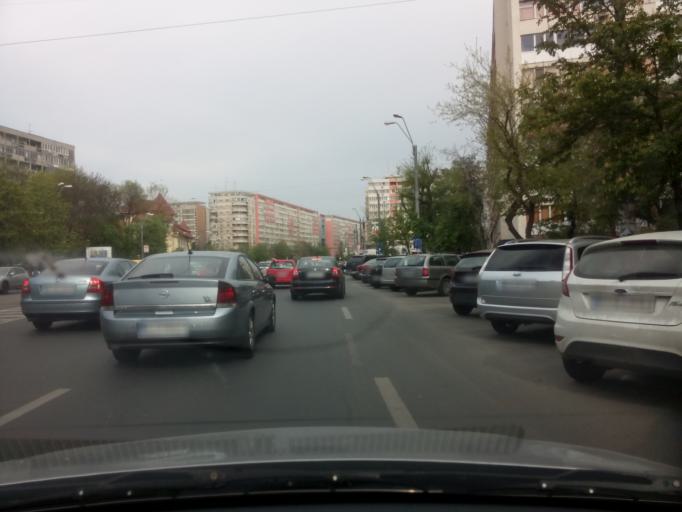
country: RO
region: Bucuresti
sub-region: Municipiul Bucuresti
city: Bucharest
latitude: 44.4430
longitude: 26.1307
